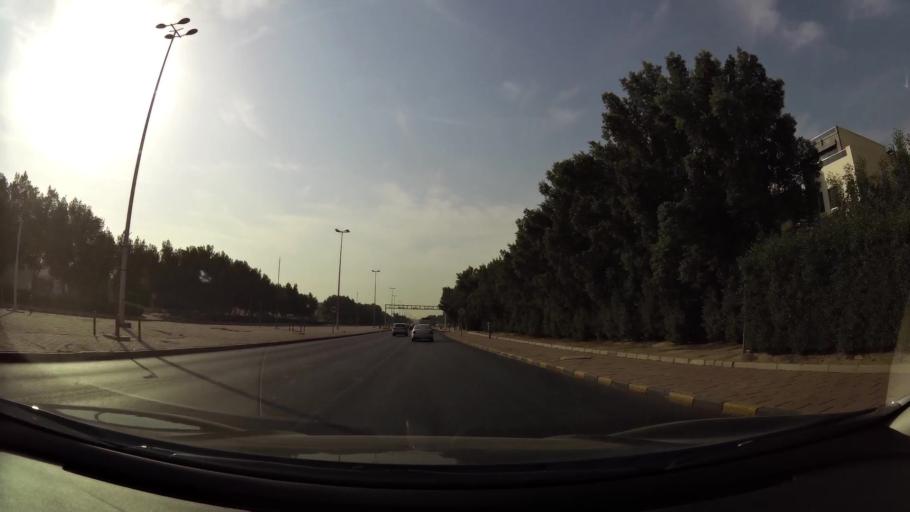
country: KW
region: Muhafazat Hawalli
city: Salwa
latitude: 29.2896
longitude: 48.0857
